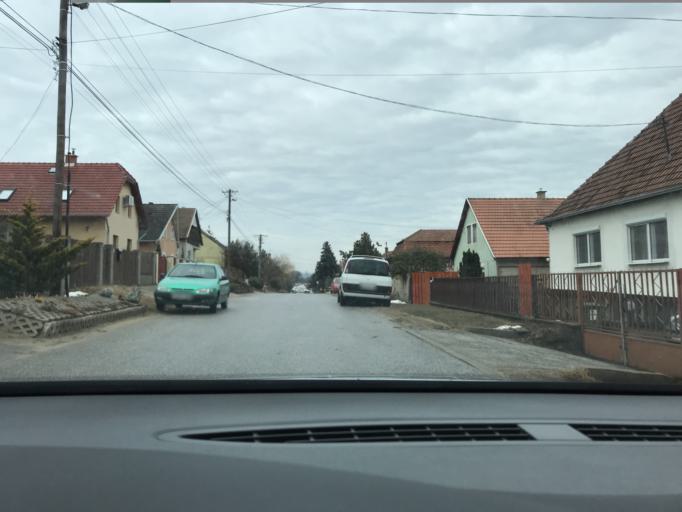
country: HU
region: Pest
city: Fot
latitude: 47.6251
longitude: 19.1760
